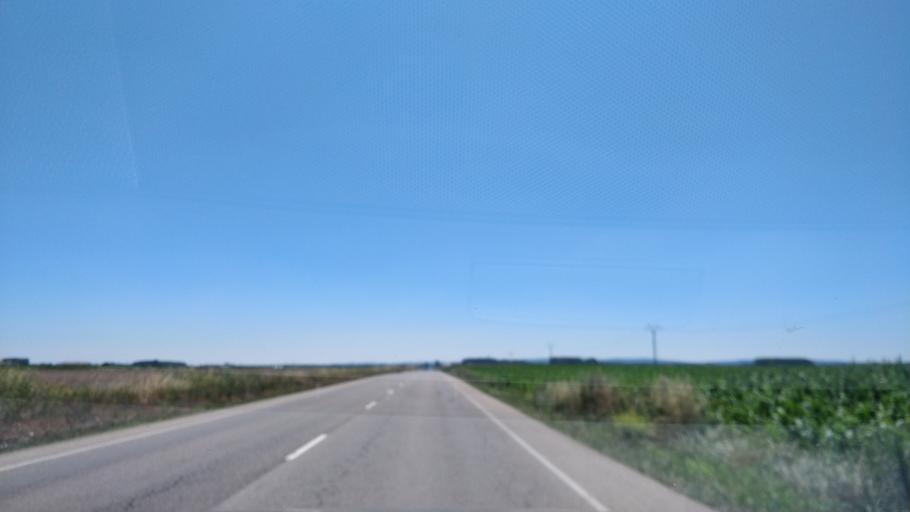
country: ES
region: Castille and Leon
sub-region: Provincia de Leon
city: Soto de la Vega
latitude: 42.3609
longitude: -5.8898
